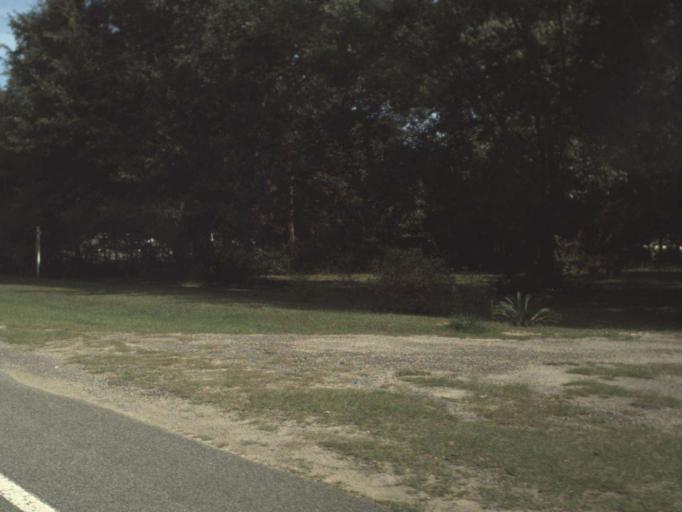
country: US
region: Florida
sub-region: Bay County
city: Lynn Haven
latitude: 30.5011
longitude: -85.6607
